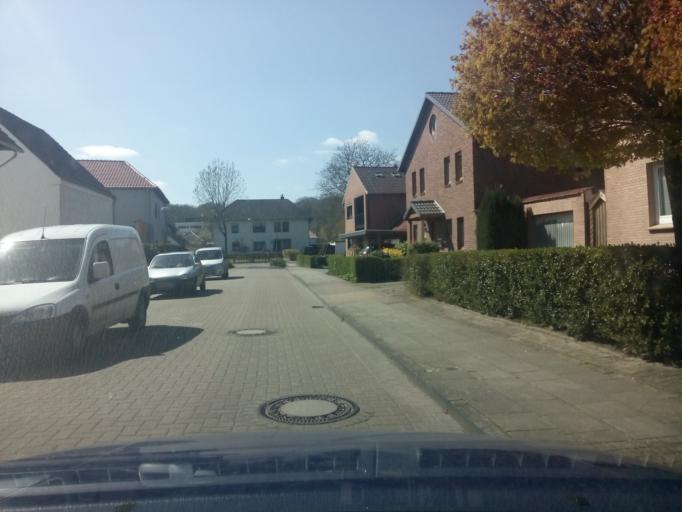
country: DE
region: Lower Saxony
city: Osterholz-Scharmbeck
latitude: 53.2284
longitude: 8.8089
